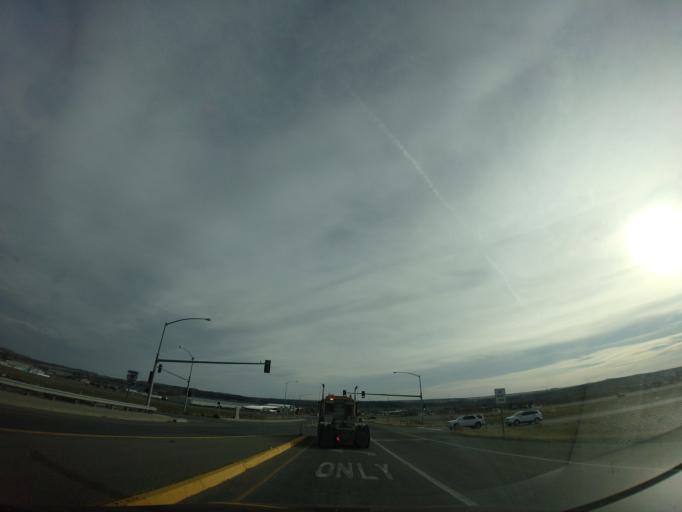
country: US
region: Montana
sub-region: Yellowstone County
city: Billings
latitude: 45.7312
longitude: -108.6029
